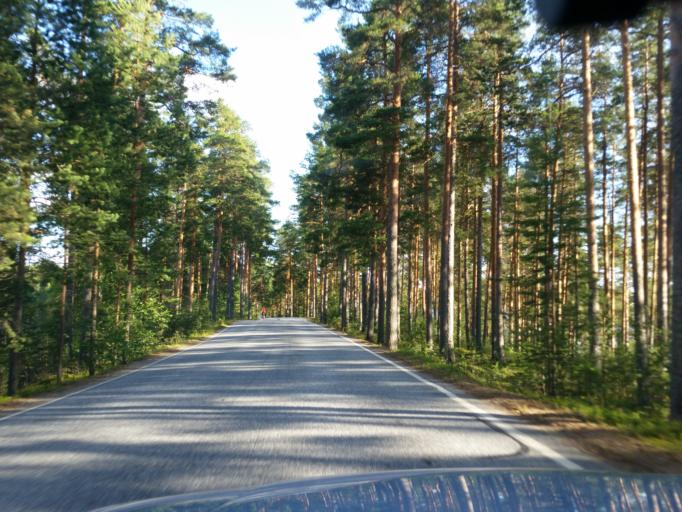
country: FI
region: Southern Savonia
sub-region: Savonlinna
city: Sulkava
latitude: 61.7758
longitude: 28.4277
